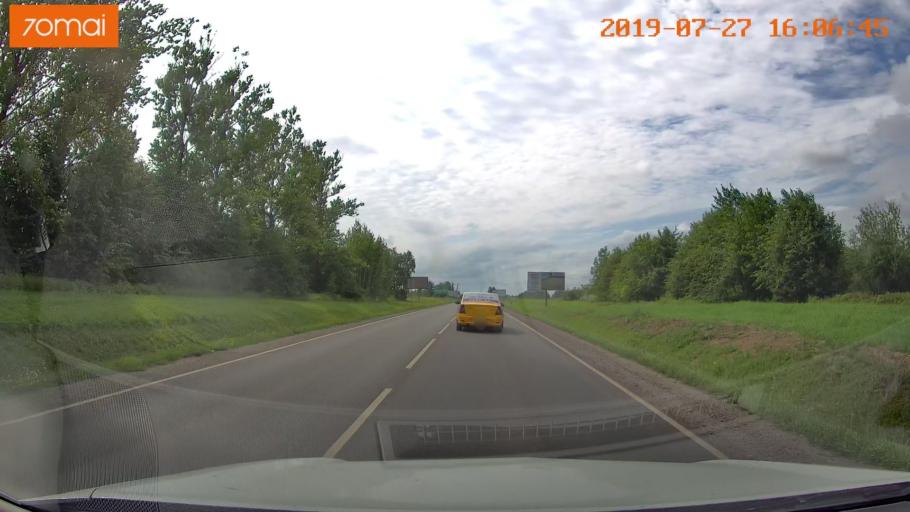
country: RU
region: Kaliningrad
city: Chernyakhovsk
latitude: 54.6343
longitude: 21.7716
